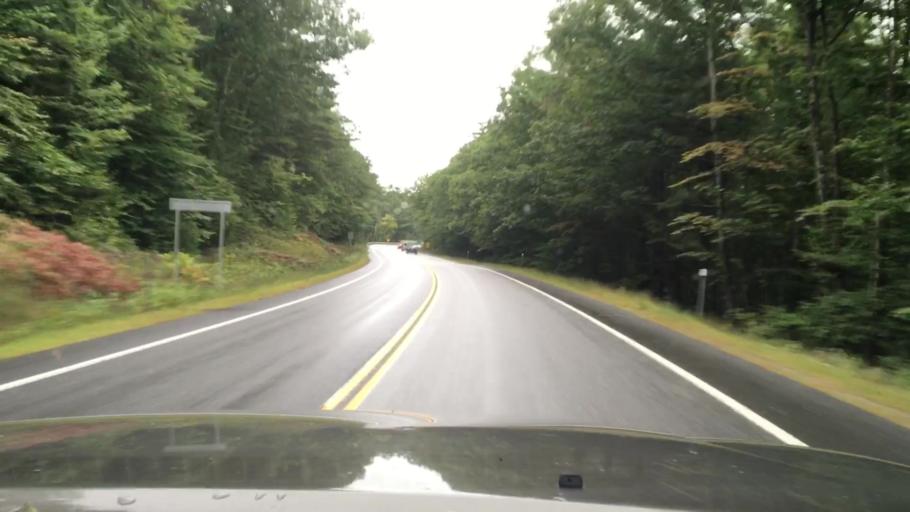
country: US
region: New Hampshire
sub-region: Hillsborough County
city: Antrim
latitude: 43.0790
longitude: -71.9793
